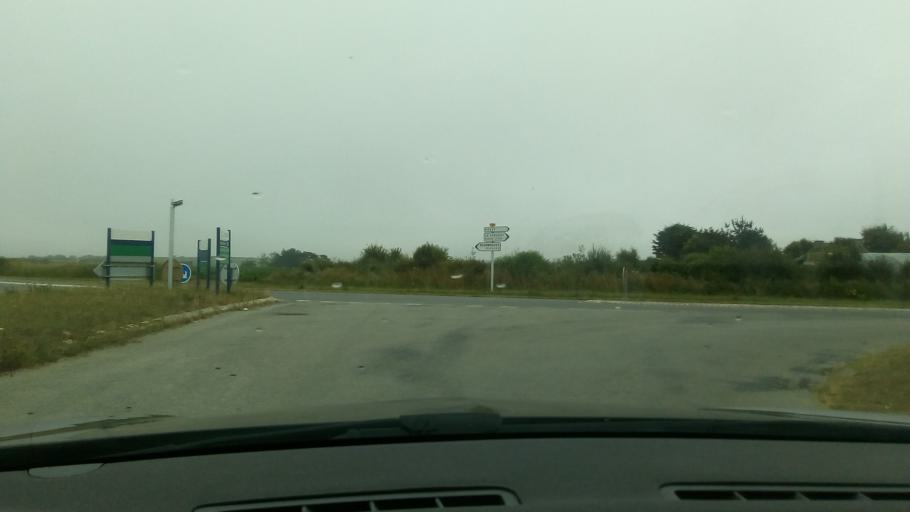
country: FR
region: Brittany
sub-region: Departement du Finistere
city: Le Conquet
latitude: 48.3759
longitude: -4.7483
